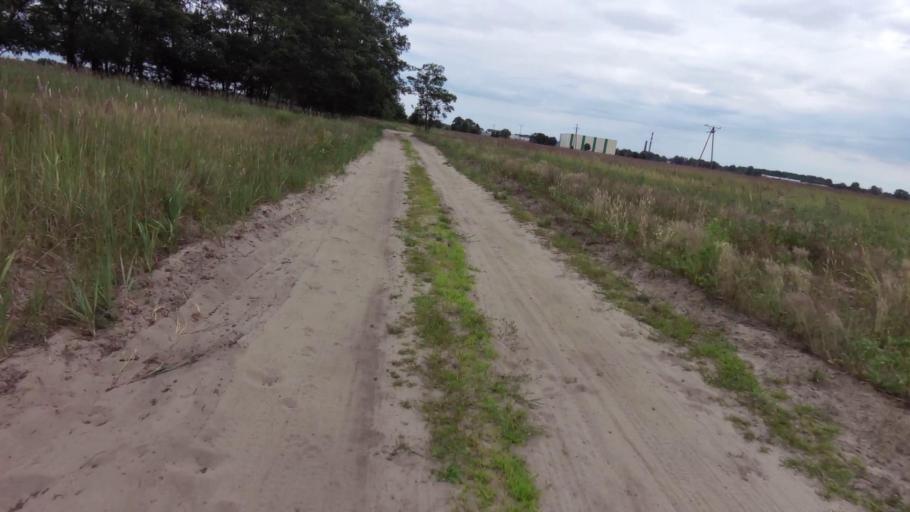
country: PL
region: Lubusz
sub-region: Powiat gorzowski
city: Kostrzyn nad Odra
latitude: 52.6130
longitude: 14.6071
